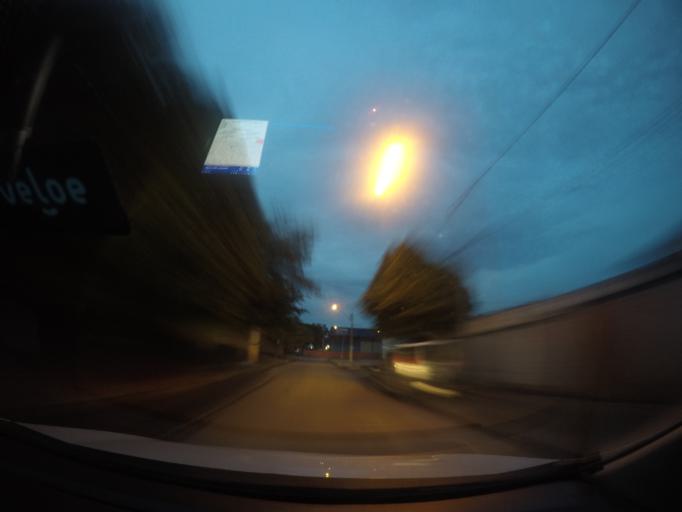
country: BR
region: Goias
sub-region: Goiania
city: Goiania
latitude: -16.6447
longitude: -49.2400
